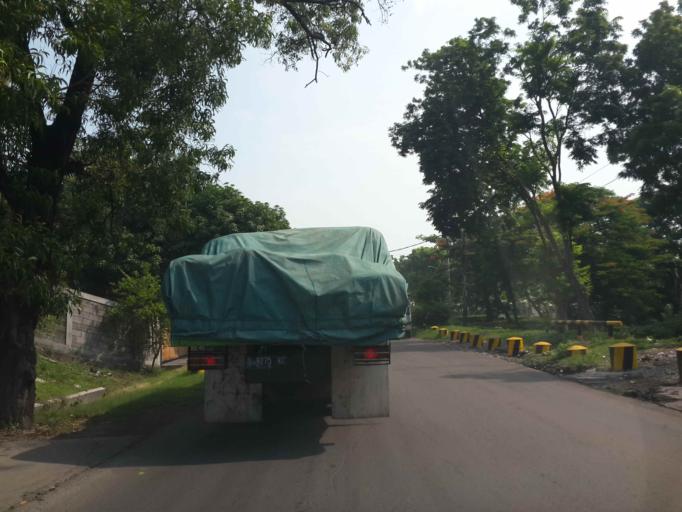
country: ID
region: East Java
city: Gresik
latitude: -7.1711
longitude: 112.6607
